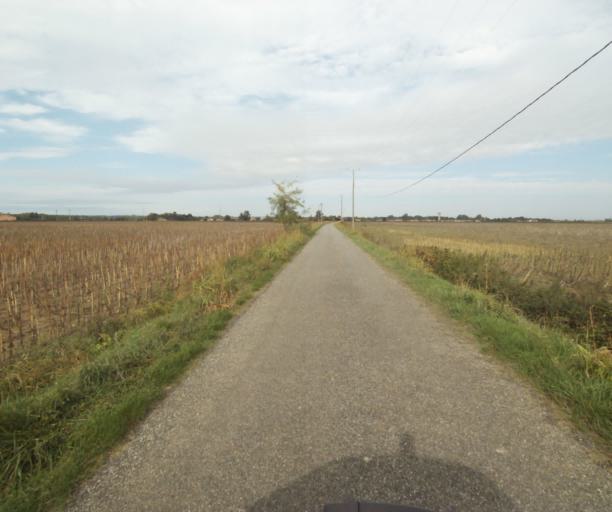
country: FR
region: Midi-Pyrenees
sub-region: Departement du Tarn-et-Garonne
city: Finhan
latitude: 43.9038
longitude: 1.2365
